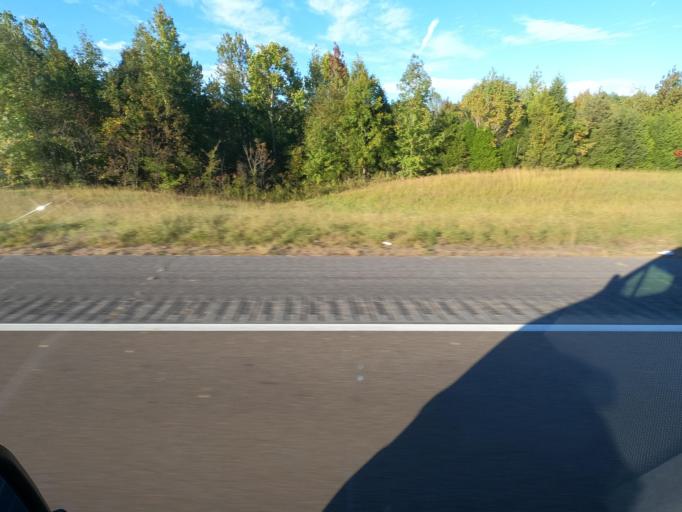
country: US
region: Tennessee
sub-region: Shelby County
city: Arlington
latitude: 35.3102
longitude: -89.7083
